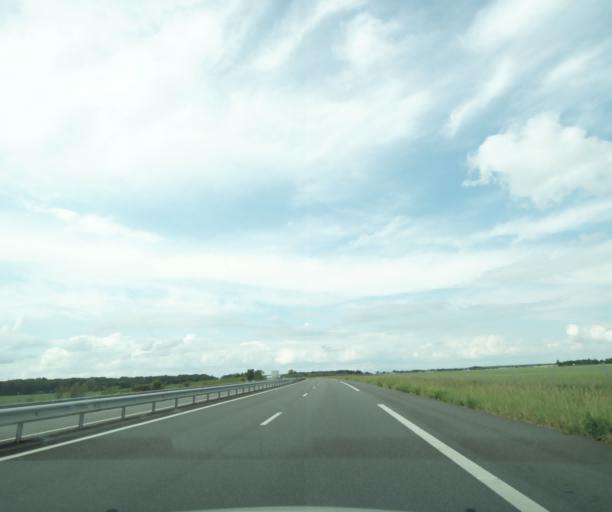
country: FR
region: Centre
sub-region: Departement du Cher
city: Levet
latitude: 46.9262
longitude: 2.4263
